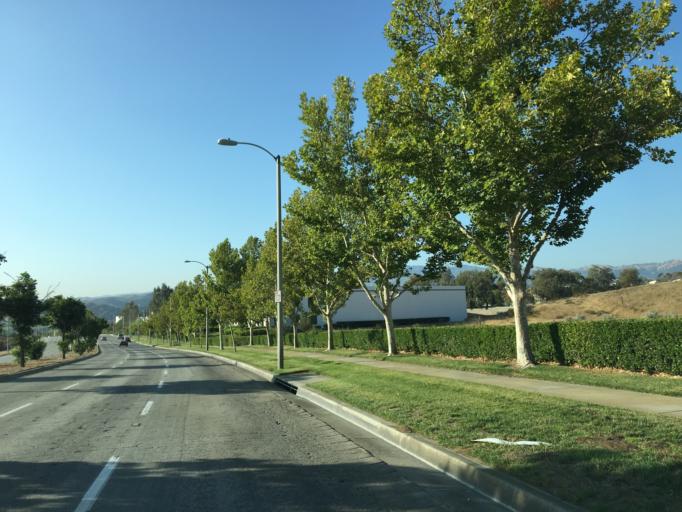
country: US
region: California
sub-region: Los Angeles County
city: Valencia
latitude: 34.4435
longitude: -118.6260
